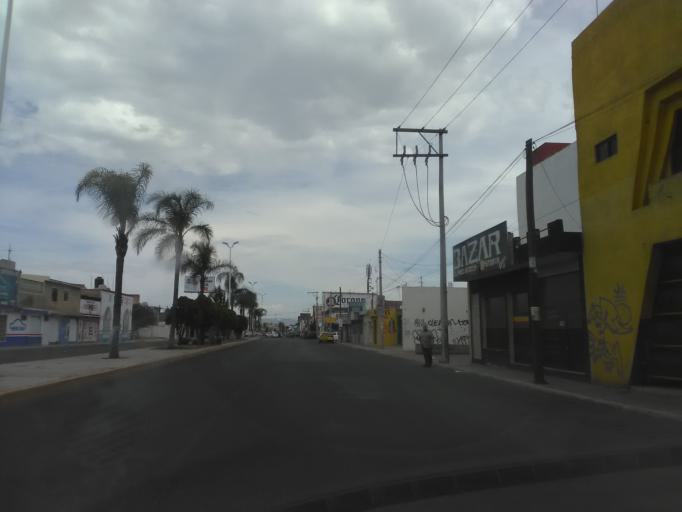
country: MX
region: Durango
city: Victoria de Durango
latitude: 24.0192
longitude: -104.6591
